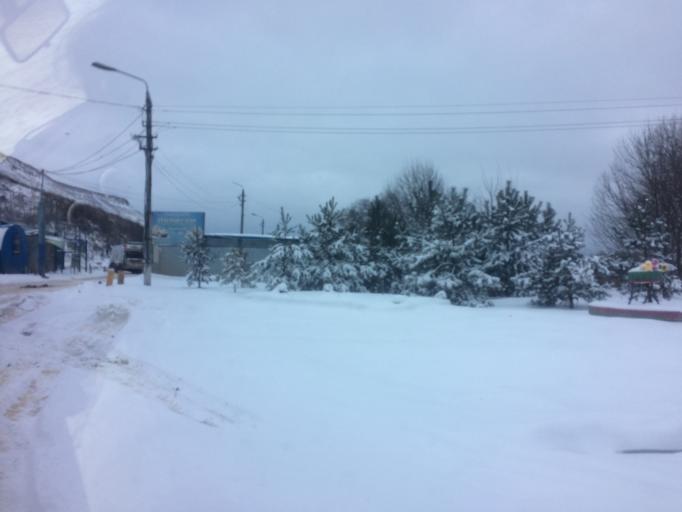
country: RU
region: Tula
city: Tula
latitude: 54.1438
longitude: 37.6549
